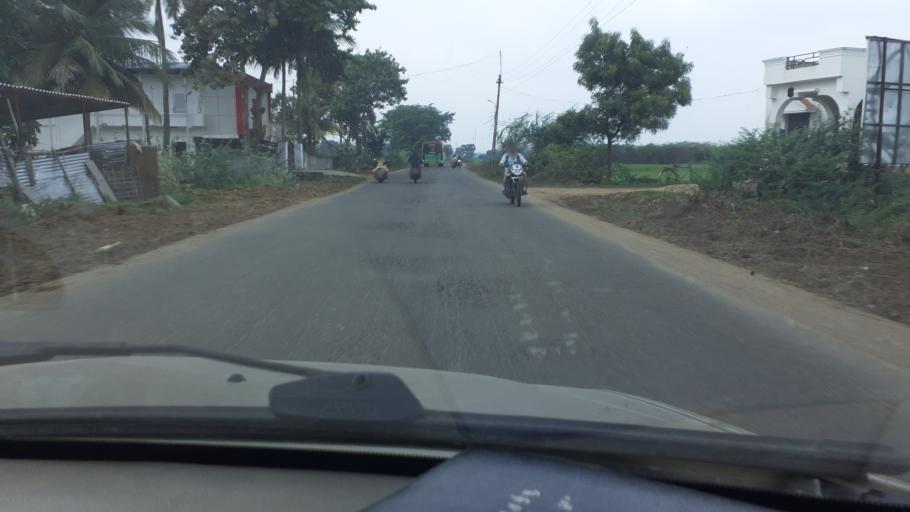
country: IN
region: Tamil Nadu
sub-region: Tirunelveli Kattabo
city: Viravanallur
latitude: 8.7232
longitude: 77.5424
